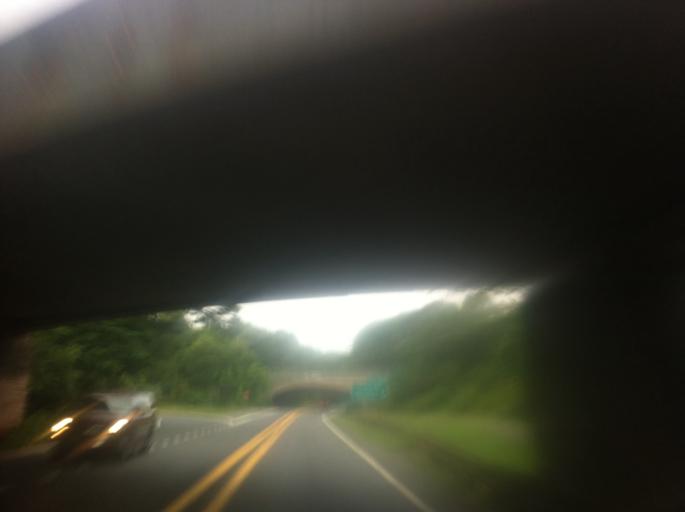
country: US
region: New York
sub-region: Nassau County
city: Plainedge
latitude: 40.7264
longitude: -73.4680
